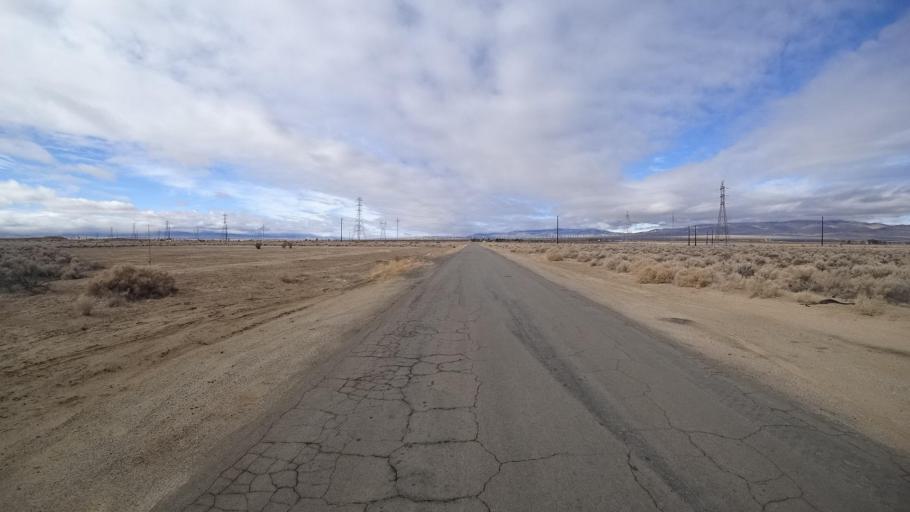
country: US
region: California
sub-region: Kern County
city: Rosamond
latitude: 34.8928
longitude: -118.2915
